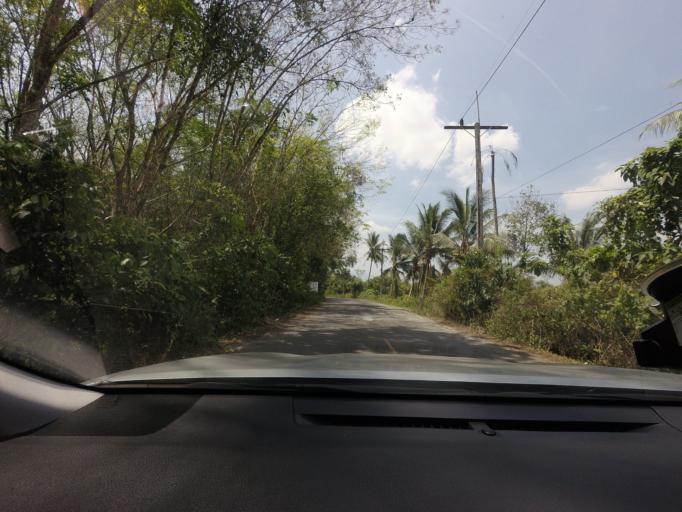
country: TH
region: Narathiwat
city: Rueso
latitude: 6.3847
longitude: 101.5081
